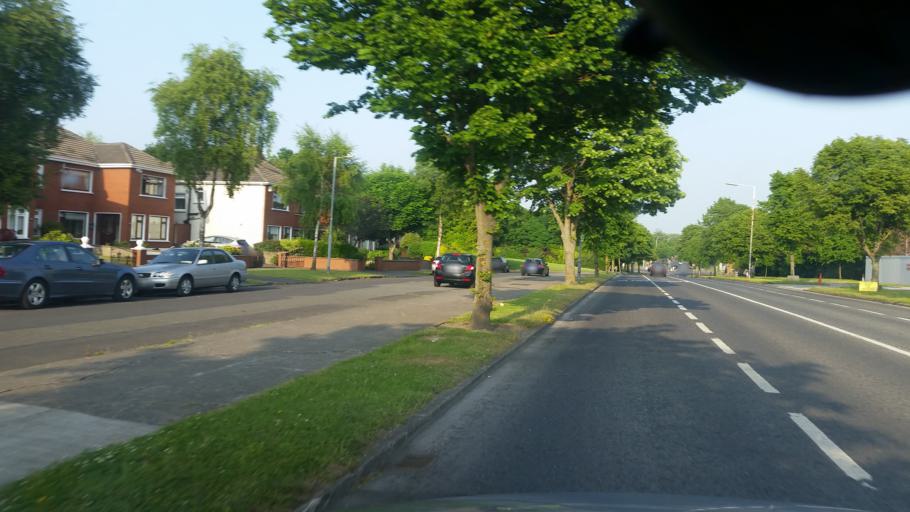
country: IE
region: Leinster
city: Glasnevin
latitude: 53.3793
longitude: -6.2708
